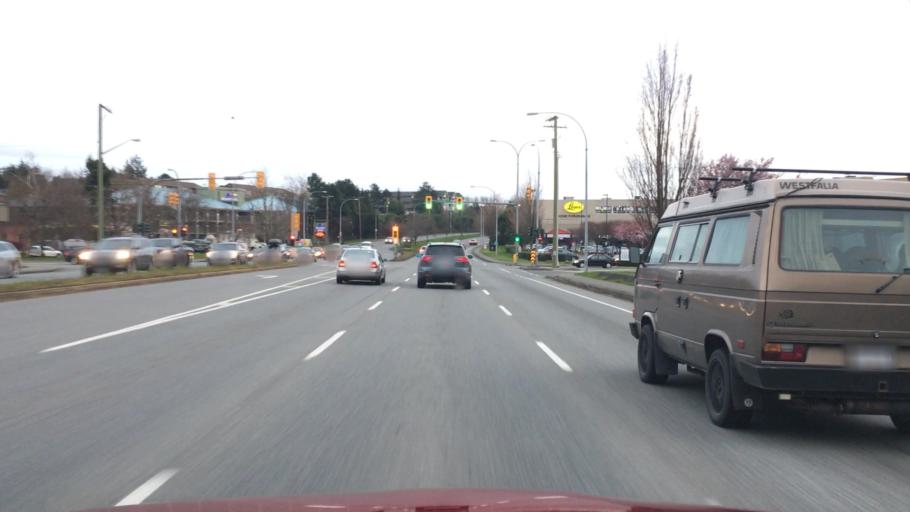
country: CA
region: British Columbia
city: Victoria
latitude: 48.4515
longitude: -123.3704
